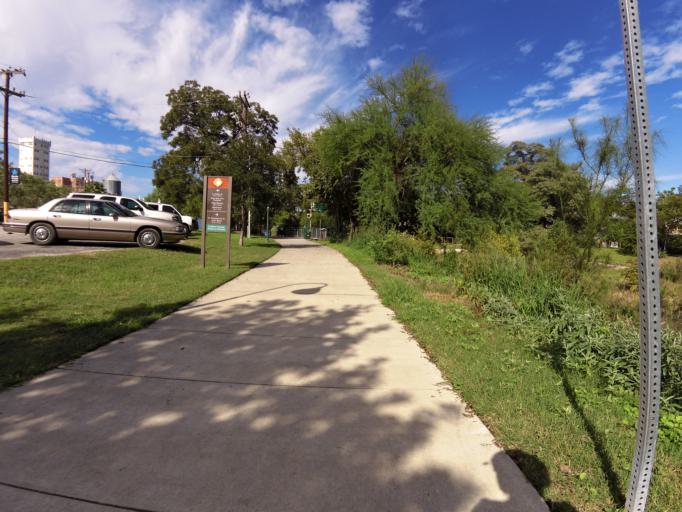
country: US
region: Texas
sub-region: Bexar County
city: San Antonio
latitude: 29.4086
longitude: -98.4947
